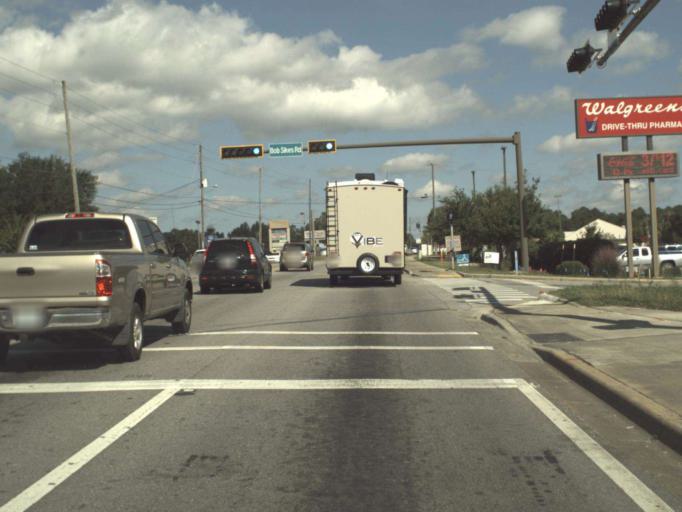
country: US
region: Florida
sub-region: Walton County
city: DeFuniak Springs
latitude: 30.7056
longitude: -86.1225
